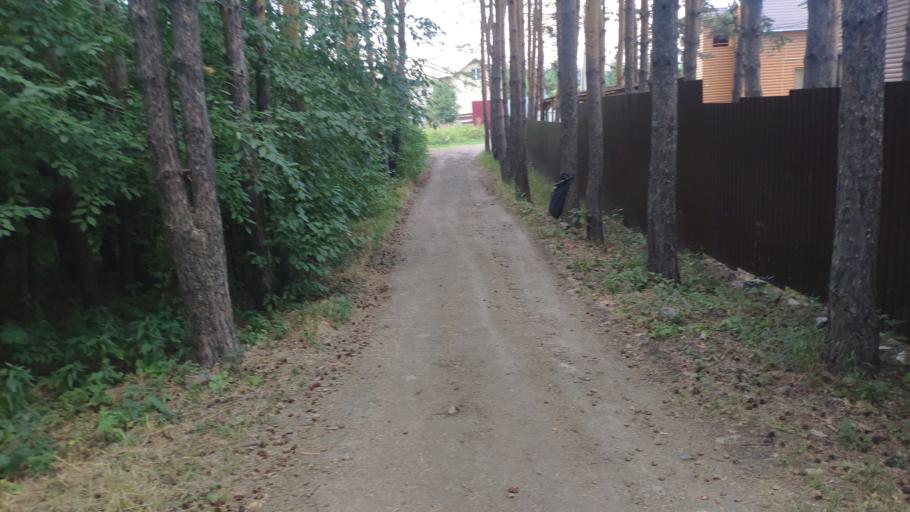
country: RU
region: Bashkortostan
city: Abzakovo
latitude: 53.8064
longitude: 58.6433
